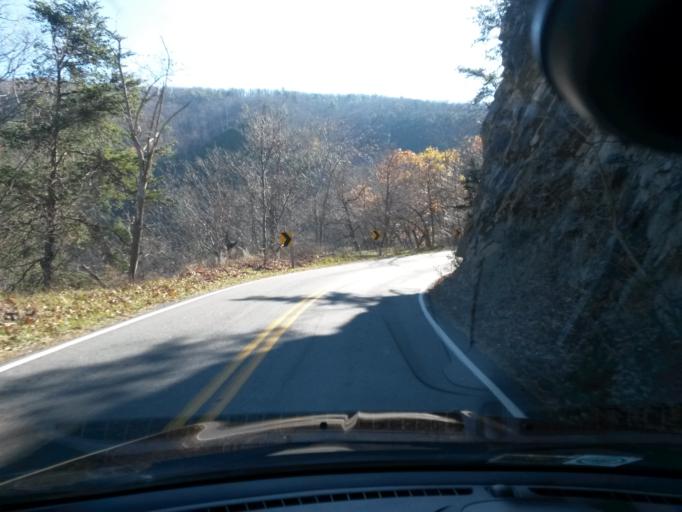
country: US
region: Virginia
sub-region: Botetourt County
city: Buchanan
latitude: 37.4956
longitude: -79.6585
